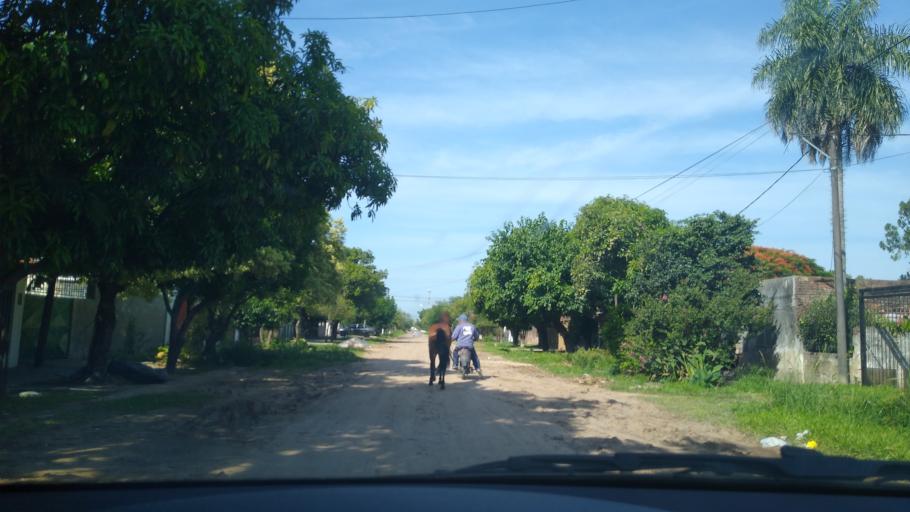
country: AR
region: Chaco
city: Barranqueras
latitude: -27.4900
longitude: -58.9493
